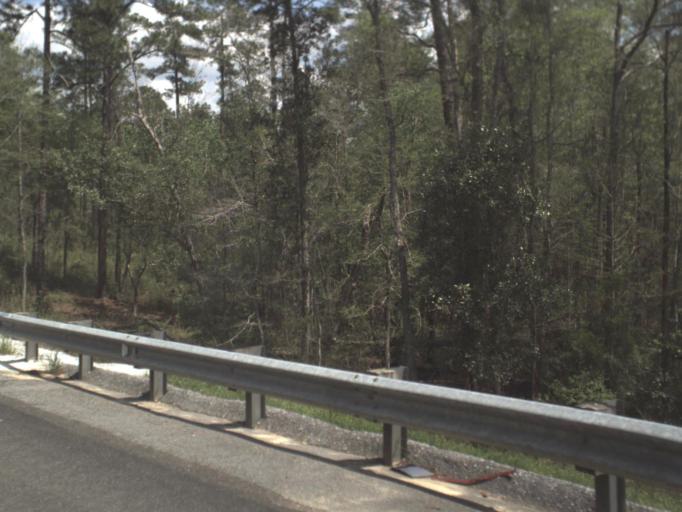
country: US
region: Florida
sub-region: Okaloosa County
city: Crestview
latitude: 30.8876
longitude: -86.6626
